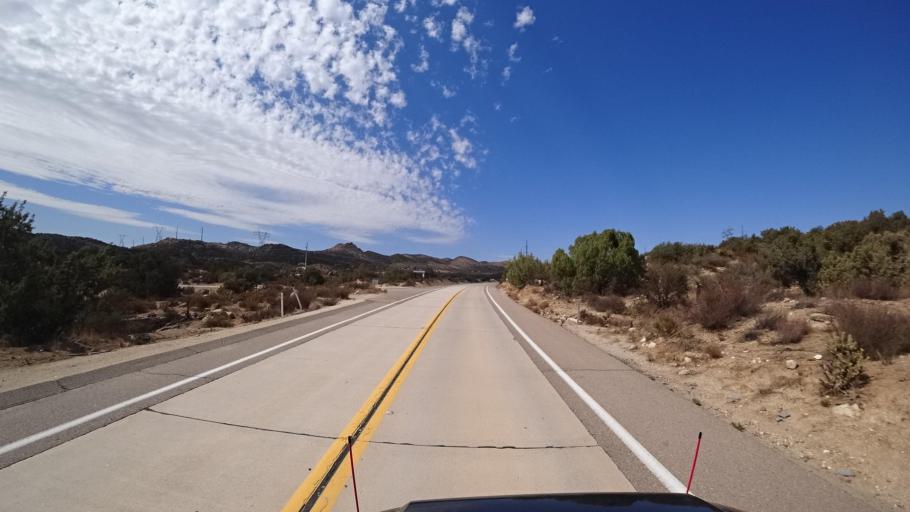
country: MX
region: Baja California
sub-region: Tecate
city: Cereso del Hongo
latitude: 32.6180
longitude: -116.2150
